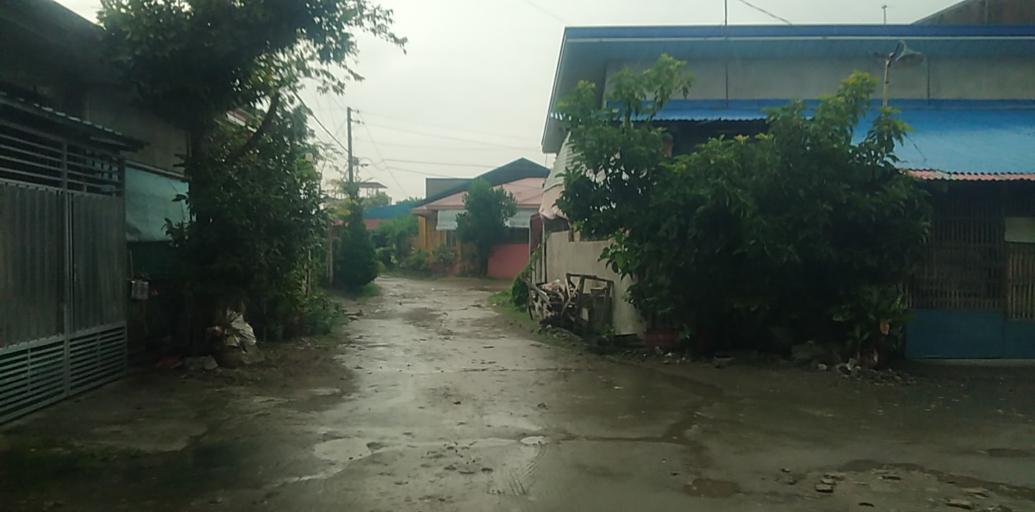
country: PH
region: Central Luzon
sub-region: Province of Pampanga
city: Arenas
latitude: 15.1722
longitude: 120.6820
